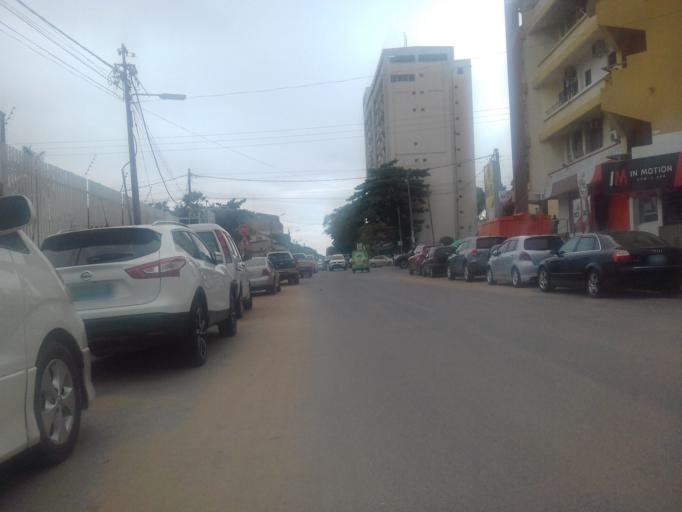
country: MZ
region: Maputo City
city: Maputo
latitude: -25.9523
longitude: 32.5869
